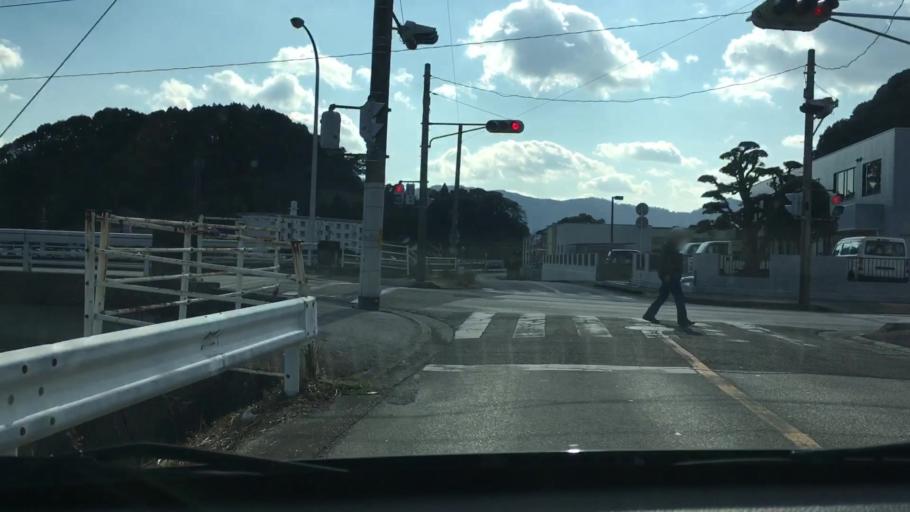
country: JP
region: Oita
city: Saiki
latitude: 32.9617
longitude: 131.9124
